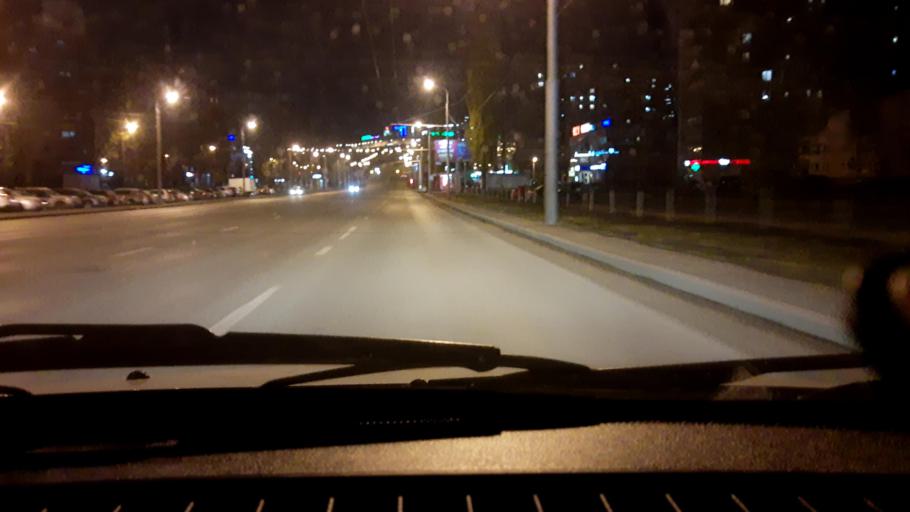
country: RU
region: Bashkortostan
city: Ufa
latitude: 54.7677
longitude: 56.0531
